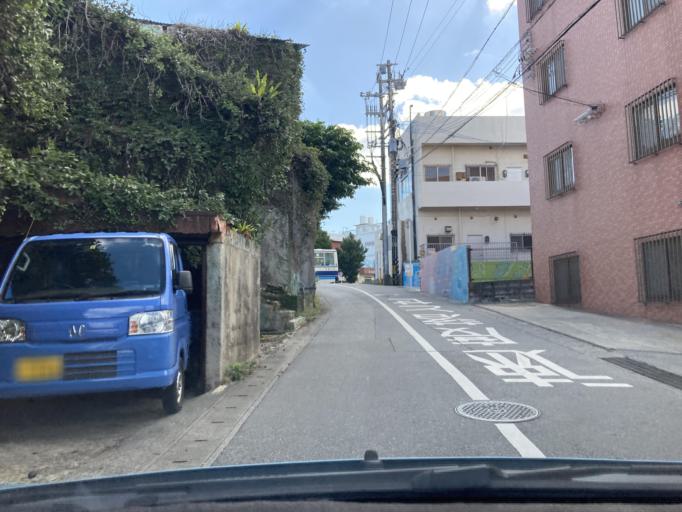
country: JP
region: Okinawa
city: Okinawa
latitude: 26.3258
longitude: 127.7927
